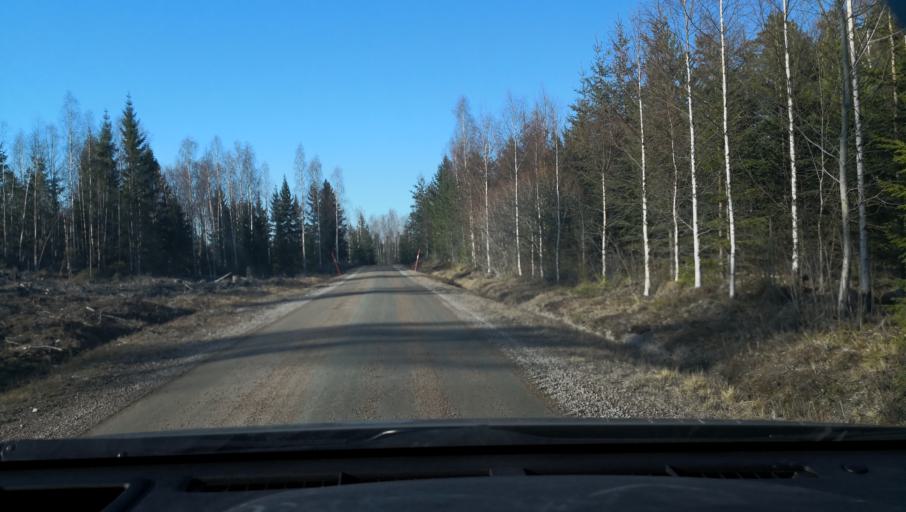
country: SE
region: Vaestmanland
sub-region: Sala Kommun
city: Sala
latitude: 60.1600
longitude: 16.6286
